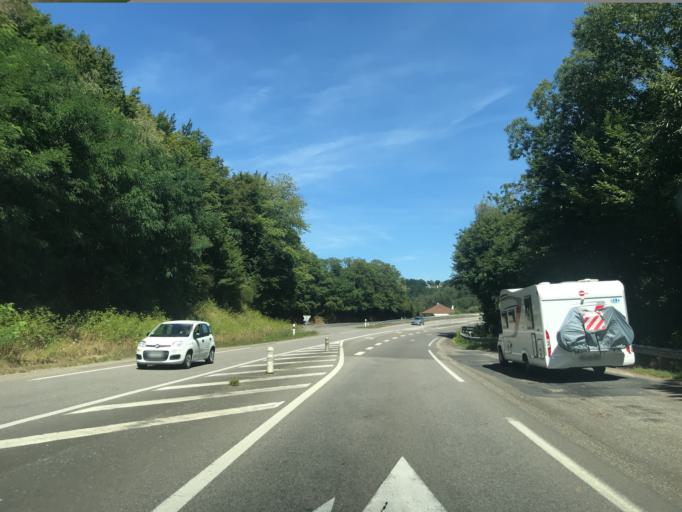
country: FR
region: Limousin
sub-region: Departement de la Correze
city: Naves
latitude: 45.2939
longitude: 1.8077
